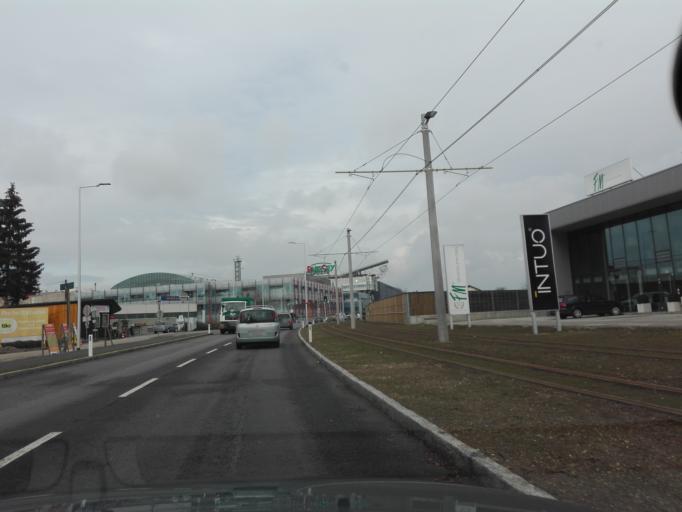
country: AT
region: Upper Austria
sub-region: Politischer Bezirk Linz-Land
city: Traun
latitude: 48.2402
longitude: 14.2347
